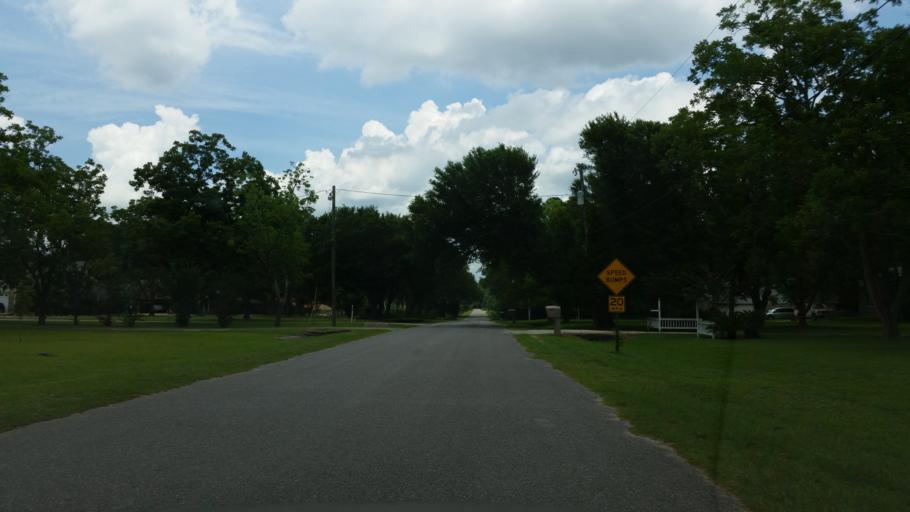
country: US
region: Florida
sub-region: Escambia County
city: Ensley
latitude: 30.5416
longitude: -87.3024
